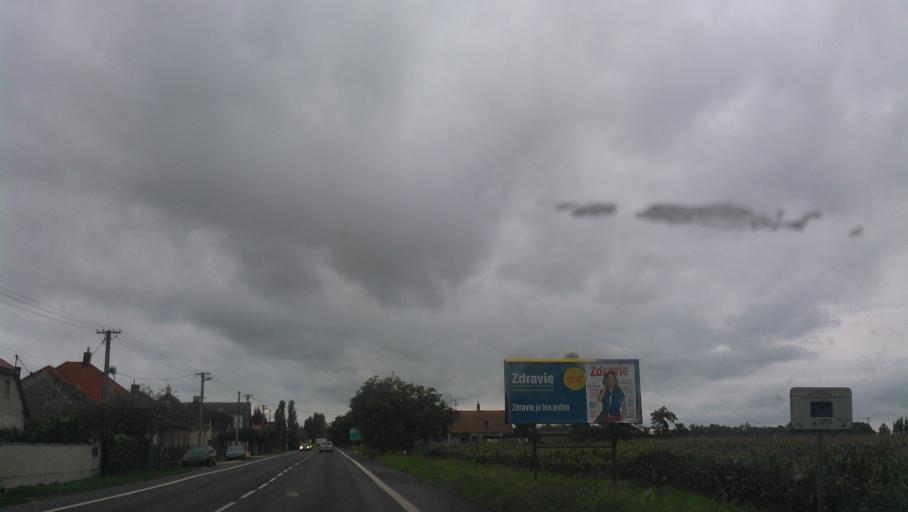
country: SK
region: Trnavsky
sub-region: Okres Dunajska Streda
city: Velky Meder
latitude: 47.9437
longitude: 17.7165
